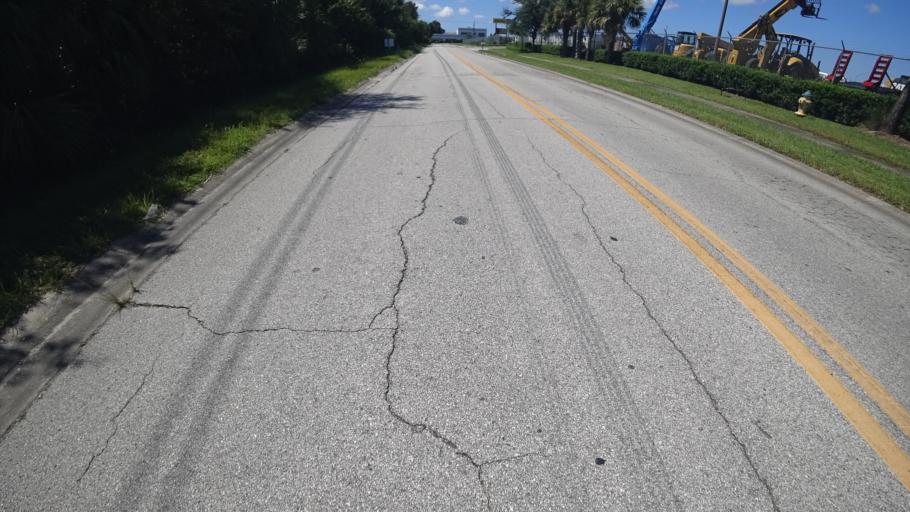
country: US
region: Florida
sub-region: Sarasota County
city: North Sarasota
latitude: 27.4057
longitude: -82.5308
